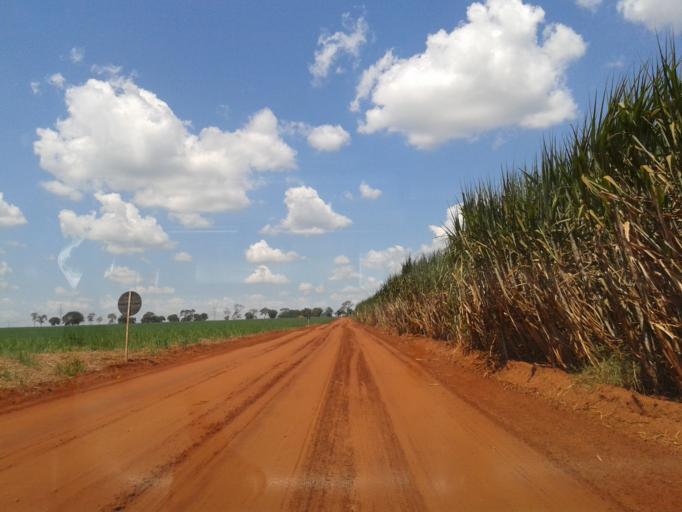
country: BR
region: Minas Gerais
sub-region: Ituiutaba
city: Ituiutaba
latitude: -18.9880
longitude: -49.6613
